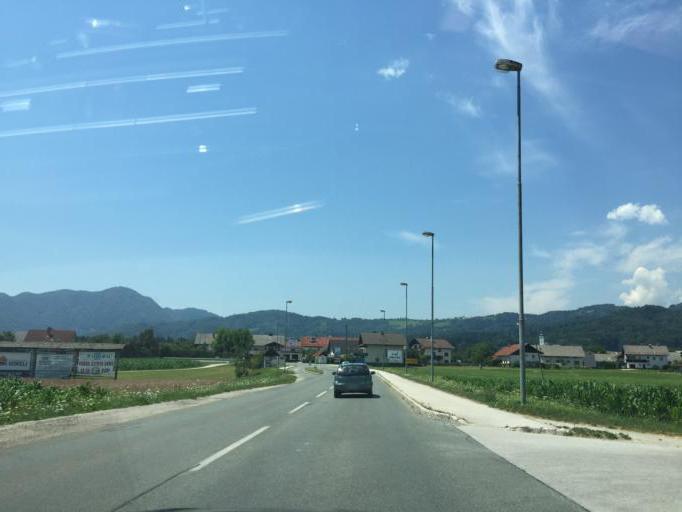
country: SI
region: Skofja Loka
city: Sv. Duh
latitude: 46.1953
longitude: 14.3274
